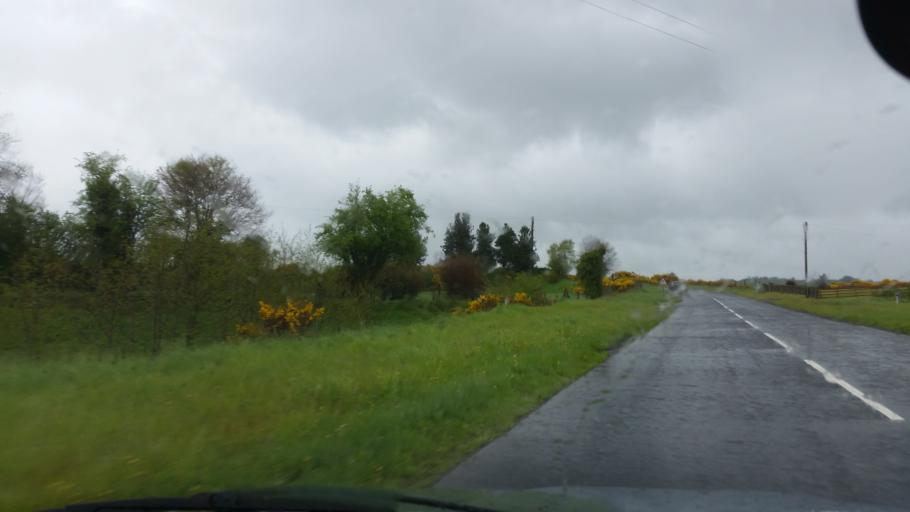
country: GB
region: Northern Ireland
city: Fintona
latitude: 54.4778
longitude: -7.3147
